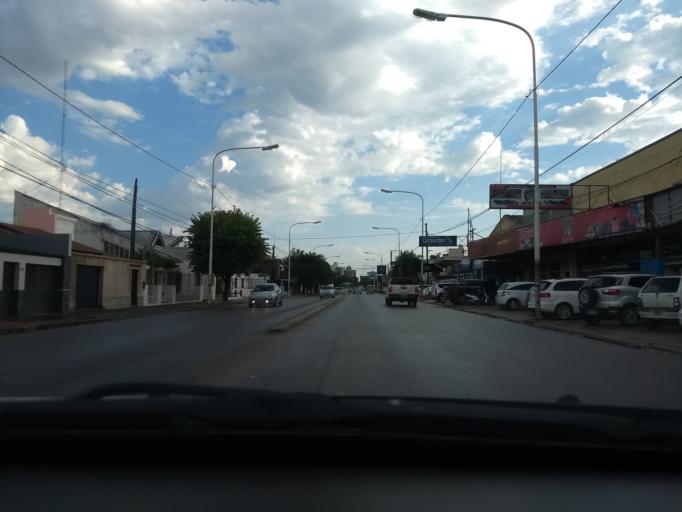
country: AR
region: Corrientes
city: Corrientes
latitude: -27.4813
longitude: -58.8272
